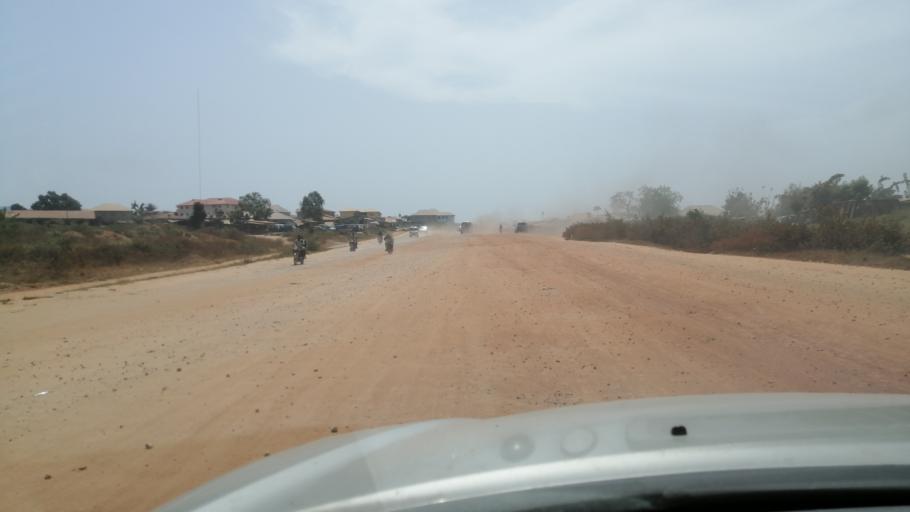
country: NG
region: Osun
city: Osogbo
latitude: 7.7876
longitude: 4.5786
